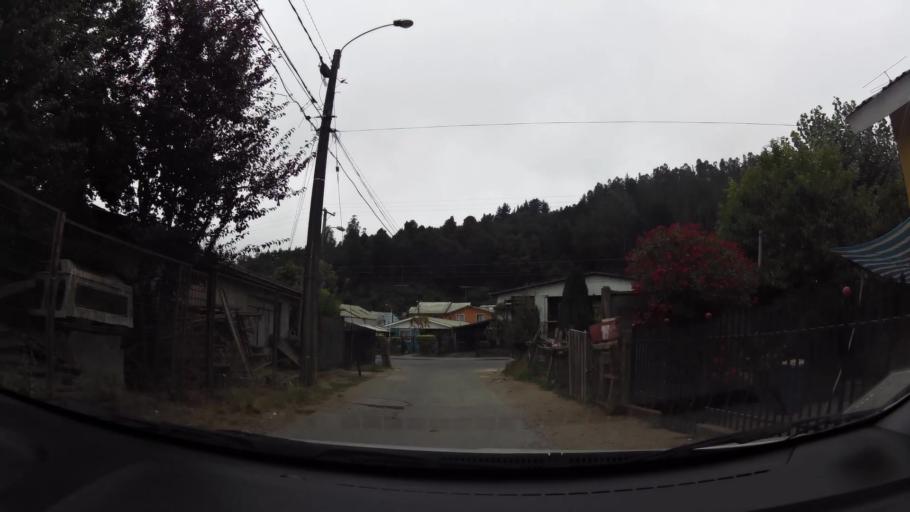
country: CL
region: Biobio
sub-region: Provincia de Concepcion
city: Concepcion
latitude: -36.8278
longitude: -72.9928
